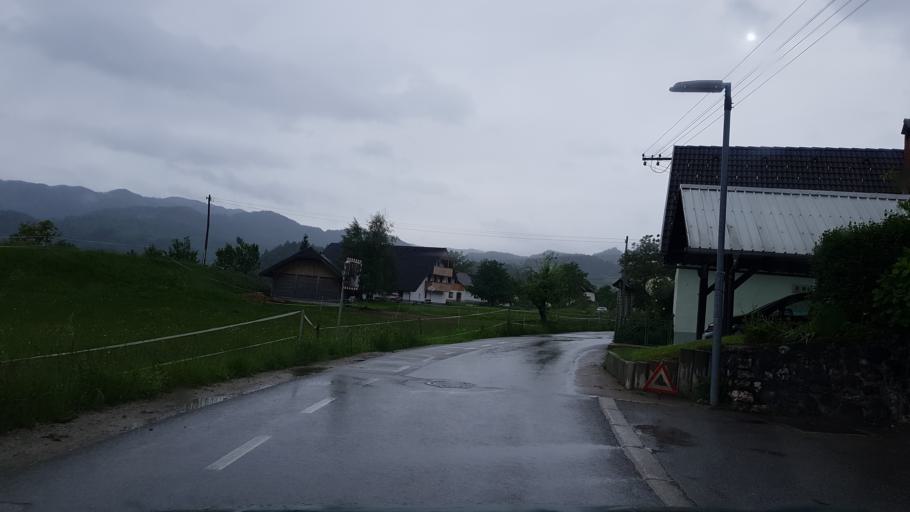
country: SI
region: Bled
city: Zasip
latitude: 46.3873
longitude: 14.1004
